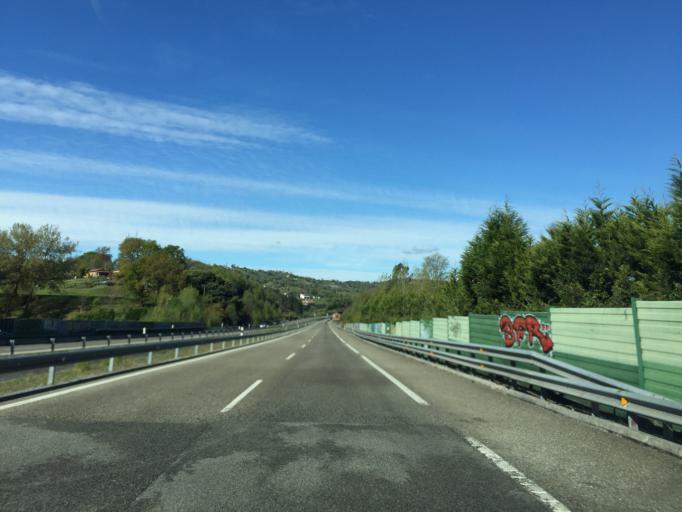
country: ES
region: Asturias
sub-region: Province of Asturias
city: Oviedo
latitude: 43.3532
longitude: -5.9182
